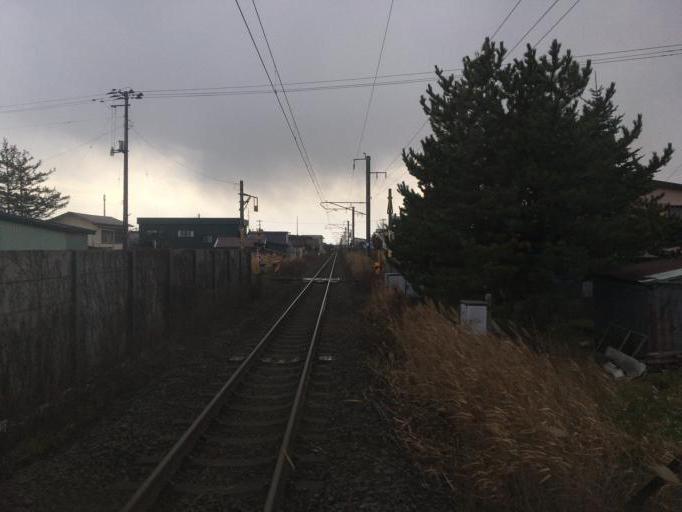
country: JP
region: Aomori
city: Aomori Shi
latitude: 40.8978
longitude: 140.6731
